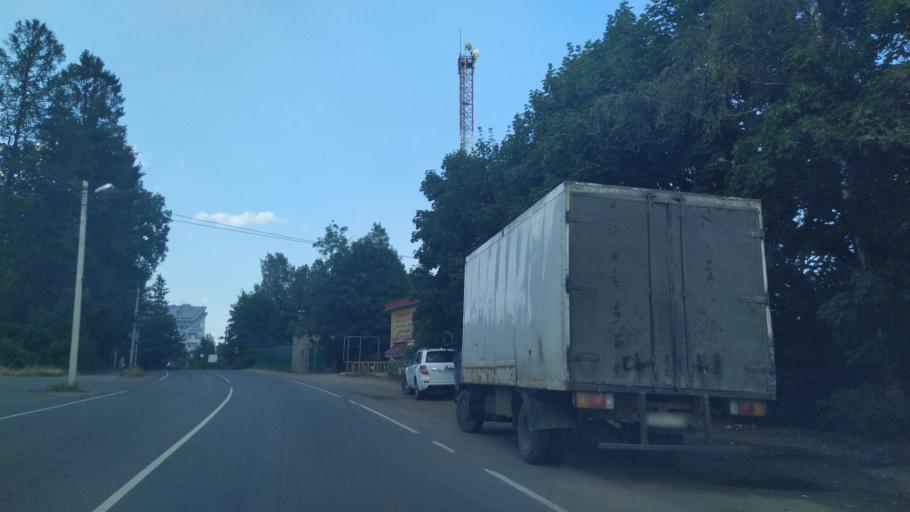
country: RU
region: Leningrad
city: Toksovo
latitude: 60.1652
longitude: 30.5417
